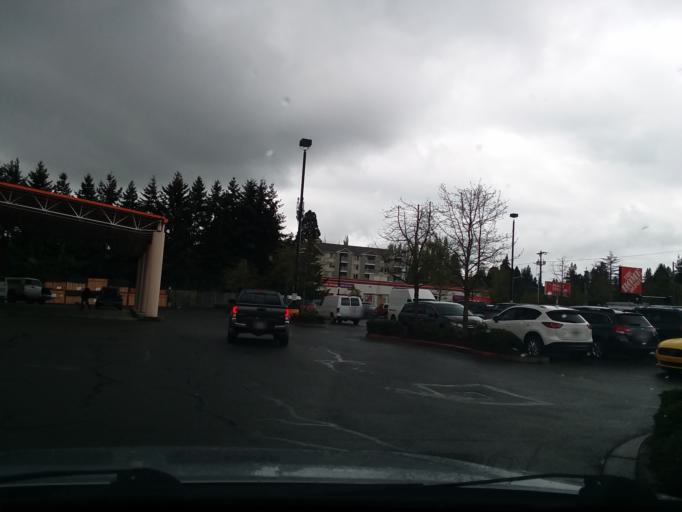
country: US
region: Washington
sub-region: King County
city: Shoreline
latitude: 47.7140
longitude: -122.3436
